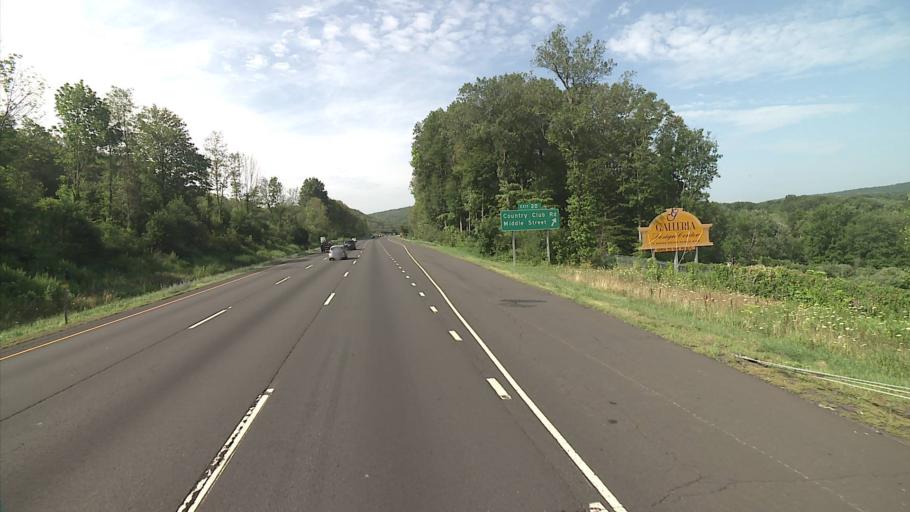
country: US
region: Connecticut
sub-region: Middlesex County
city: Middletown
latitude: 41.5757
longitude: -72.7204
